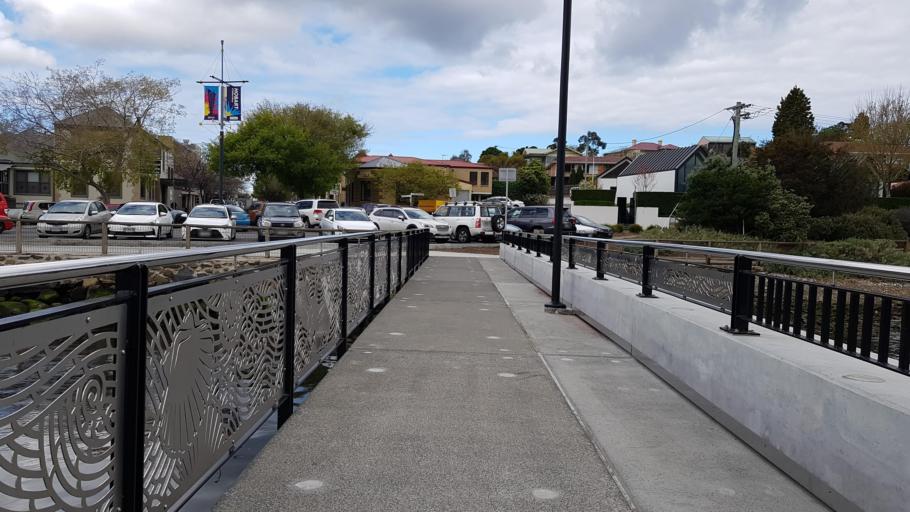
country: AU
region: Tasmania
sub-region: Clarence
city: Bellerive
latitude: -42.8740
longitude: 147.3648
